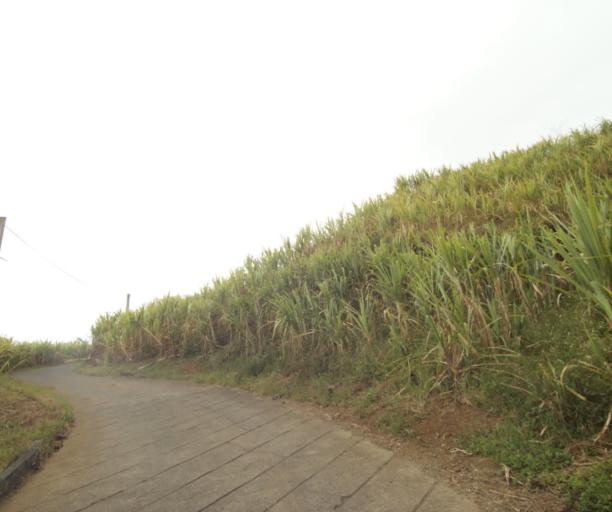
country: RE
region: Reunion
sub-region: Reunion
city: Saint-Paul
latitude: -21.0068
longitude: 55.3480
